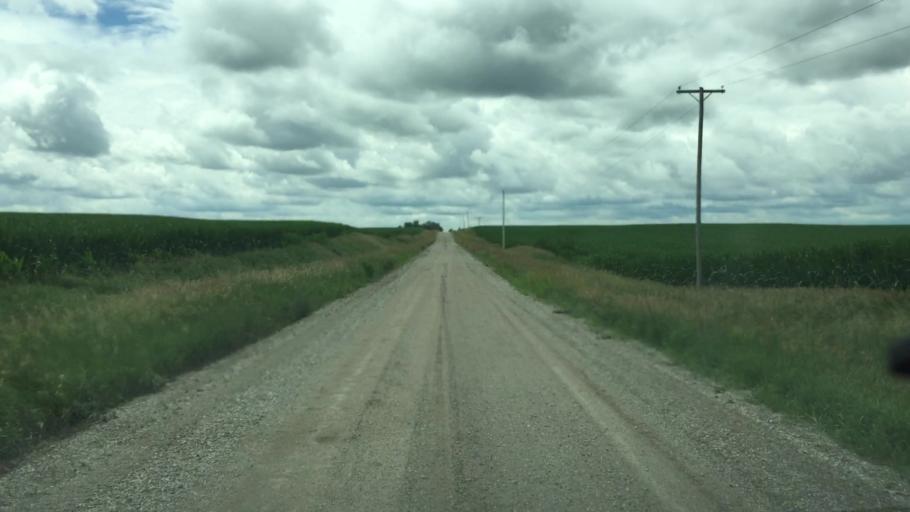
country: US
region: Iowa
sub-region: Jasper County
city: Prairie City
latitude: 41.5865
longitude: -93.1596
